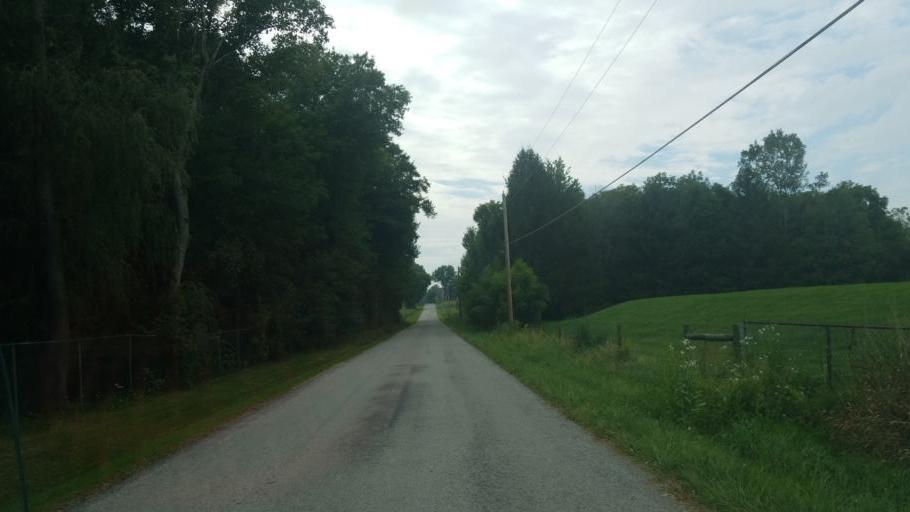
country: US
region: Ohio
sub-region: Wayne County
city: Smithville
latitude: 40.9083
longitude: -81.9381
